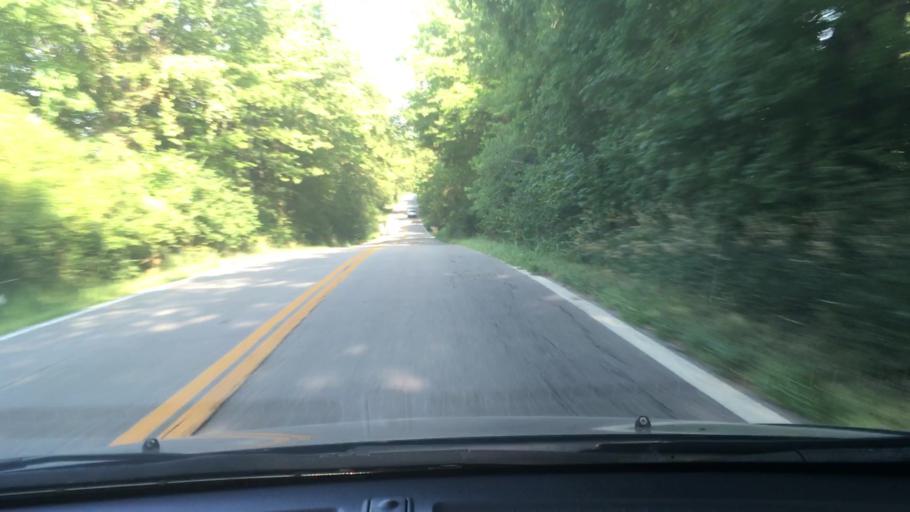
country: US
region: Missouri
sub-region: Jackson County
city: Lees Summit
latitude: 38.8906
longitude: -94.4273
